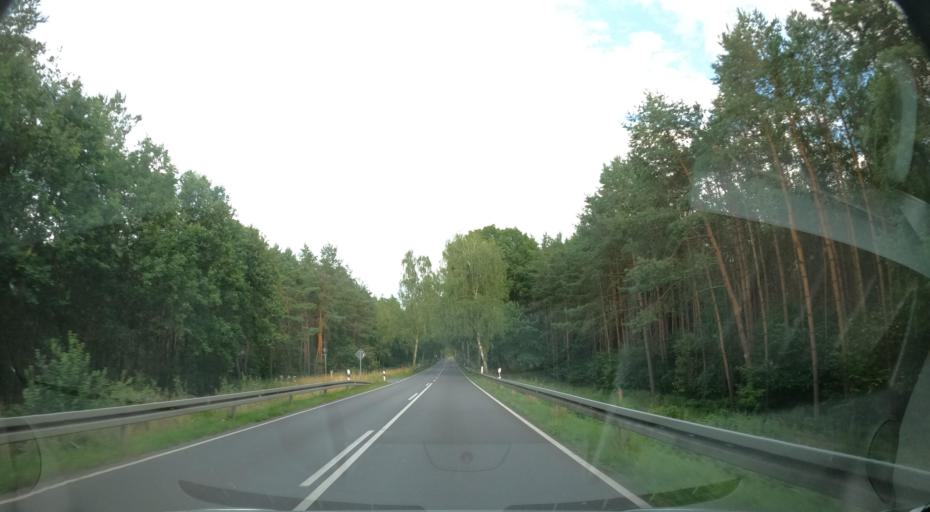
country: PL
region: West Pomeranian Voivodeship
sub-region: Powiat policki
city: Dobra
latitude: 53.4539
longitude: 14.3510
